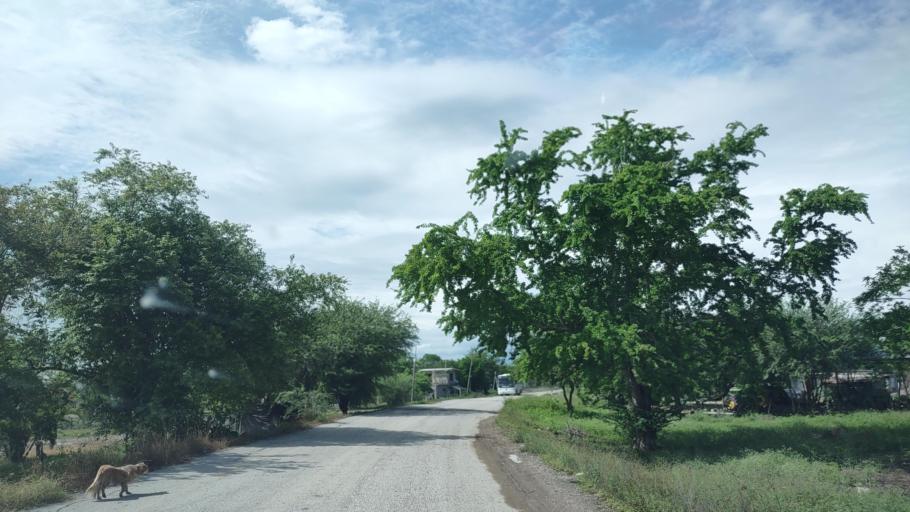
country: MX
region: Veracruz
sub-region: Panuco
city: Oviedo
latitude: 22.0044
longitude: -98.4617
